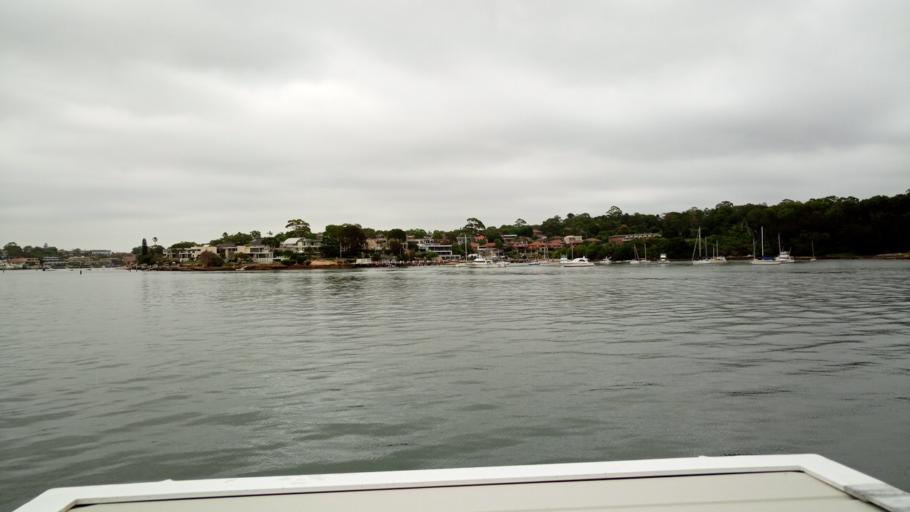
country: AU
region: New South Wales
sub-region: Canada Bay
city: Canada Bay
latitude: -33.8449
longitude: 151.1426
